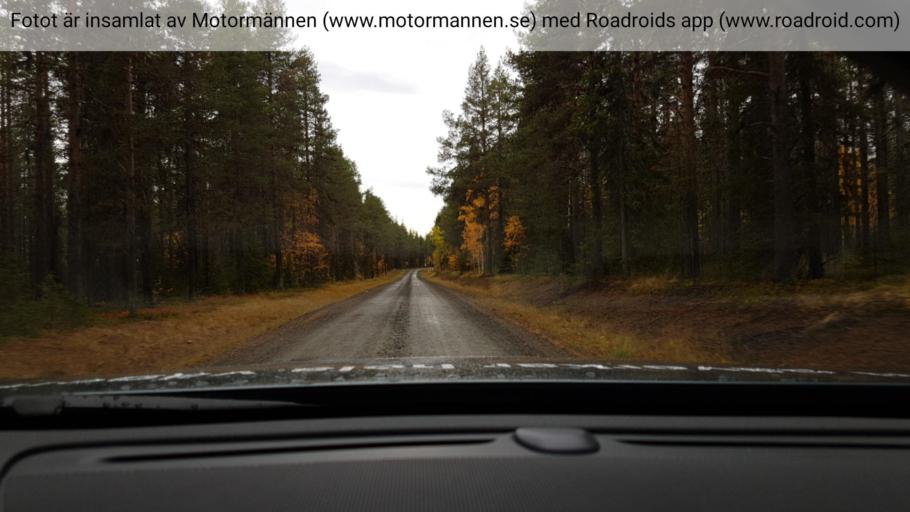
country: SE
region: Norrbotten
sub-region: Pajala Kommun
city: Pajala
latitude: 67.1267
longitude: 22.6680
